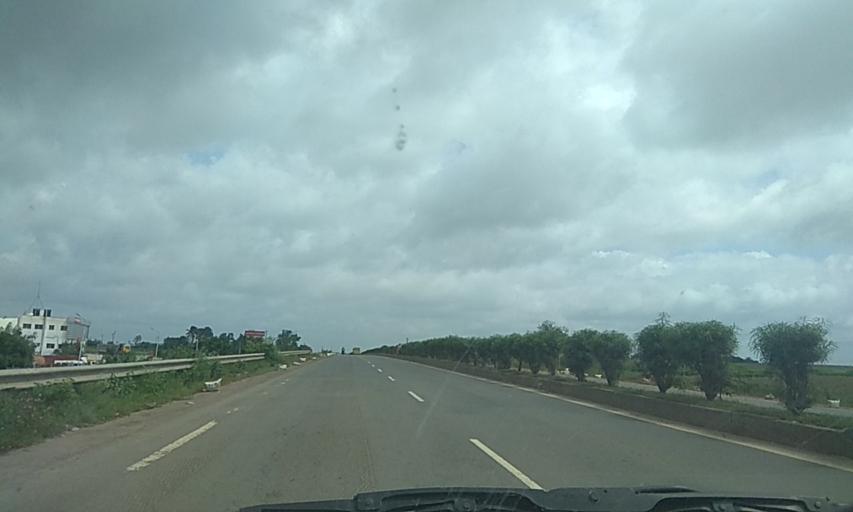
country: IN
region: Karnataka
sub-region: Dharwad
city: Hubli
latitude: 15.2486
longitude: 75.1451
